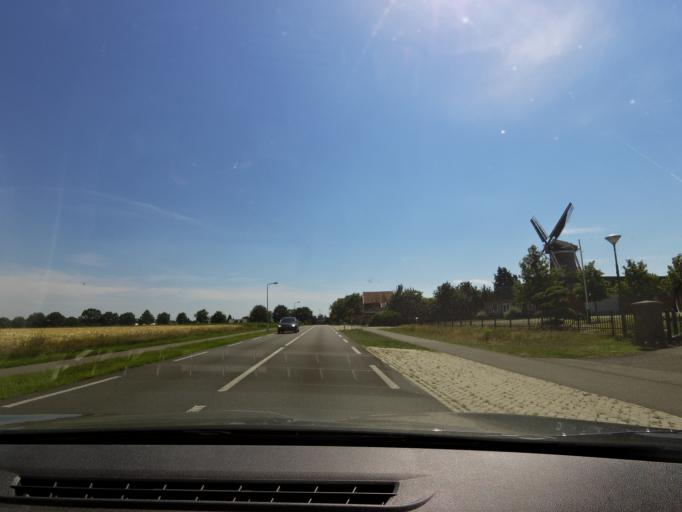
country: NL
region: Gelderland
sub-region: Berkelland
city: Neede
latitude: 52.1426
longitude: 6.6108
